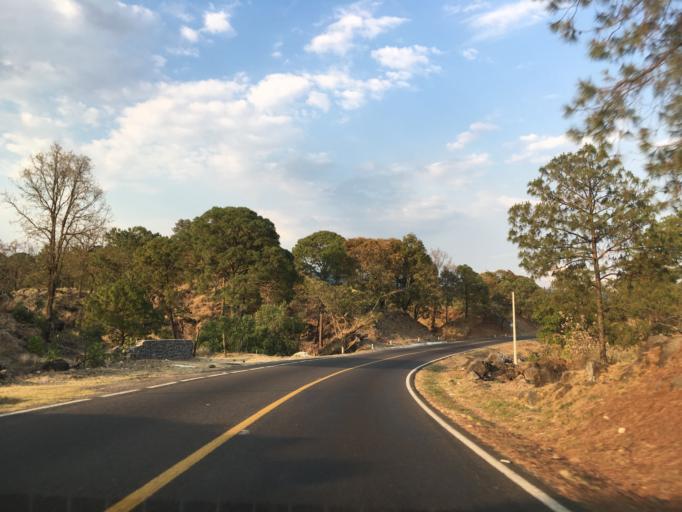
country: MX
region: Michoacan
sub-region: Uruapan
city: Toreo Bajo (El Toreo Bajo)
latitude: 19.4536
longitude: -101.9609
